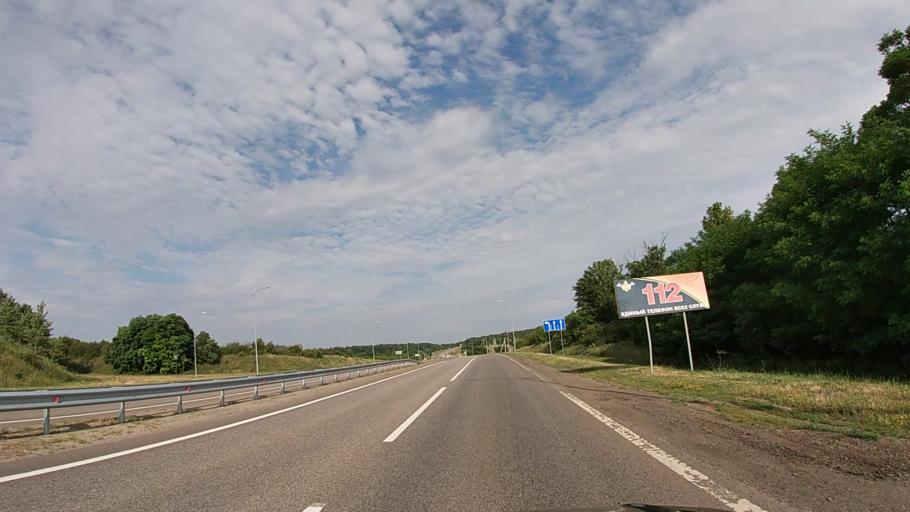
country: RU
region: Belgorod
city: Tomarovka
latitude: 50.6610
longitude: 36.3492
